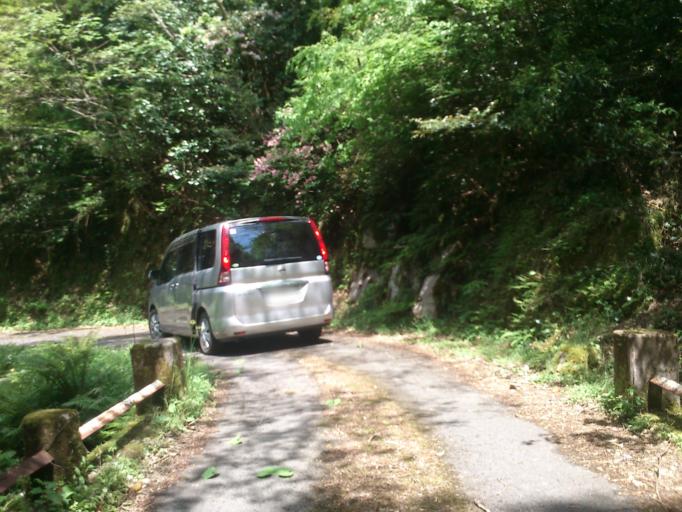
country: JP
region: Kyoto
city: Miyazu
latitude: 35.7024
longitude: 135.1197
